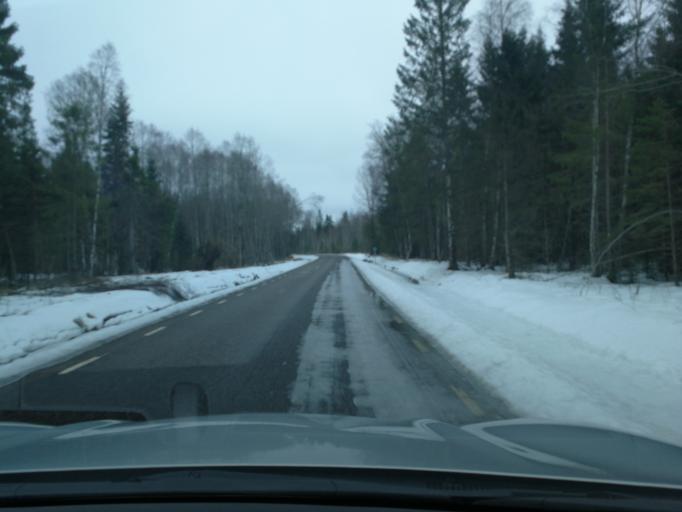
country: EE
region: Harju
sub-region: Rae vald
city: Vaida
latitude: 59.2325
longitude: 24.9420
